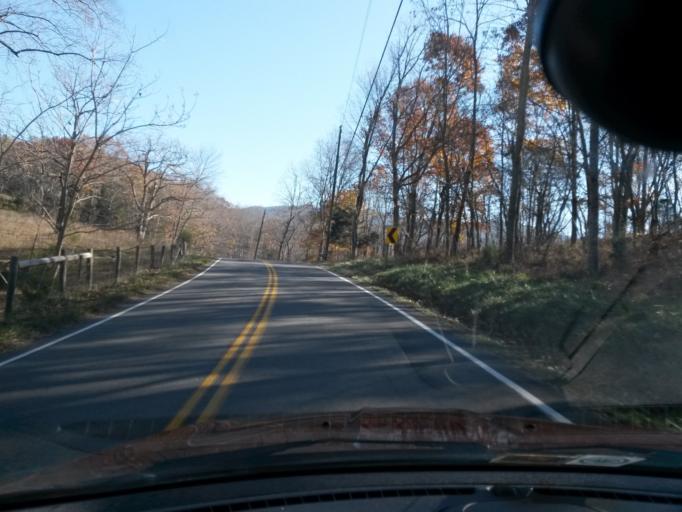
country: US
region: Virginia
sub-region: Botetourt County
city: Buchanan
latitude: 37.6372
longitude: -79.7405
